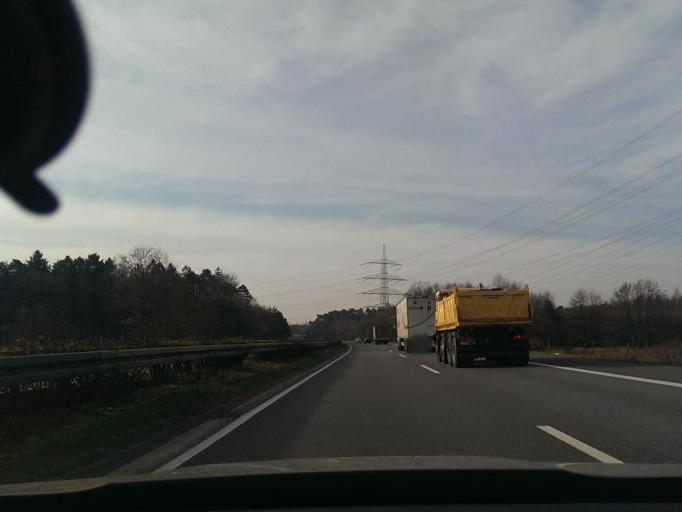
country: DE
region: North Rhine-Westphalia
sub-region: Regierungsbezirk Detmold
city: Oerlinghausen
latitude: 51.9148
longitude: 8.6187
